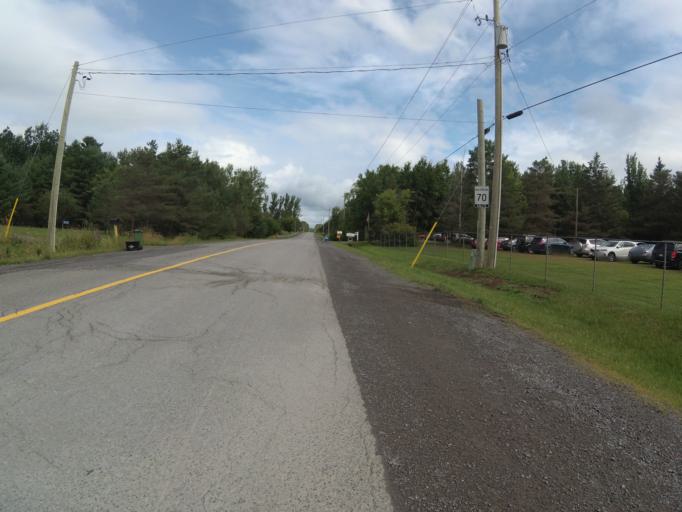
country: CA
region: Ontario
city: Clarence-Rockland
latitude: 45.4899
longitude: -75.3142
